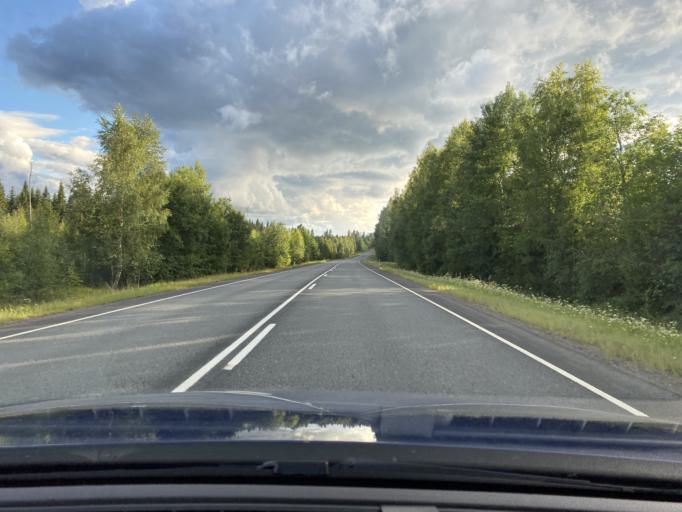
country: FI
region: Haeme
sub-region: Haemeenlinna
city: Renko
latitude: 60.8526
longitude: 24.1575
